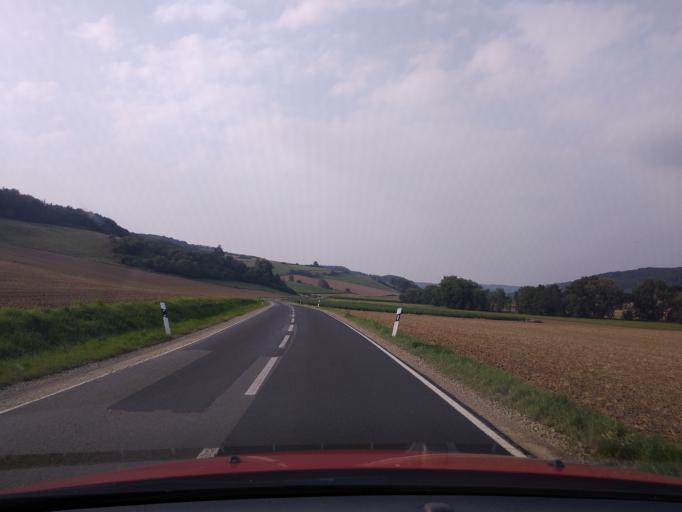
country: DE
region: Hesse
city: Liebenau
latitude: 51.4670
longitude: 9.3017
